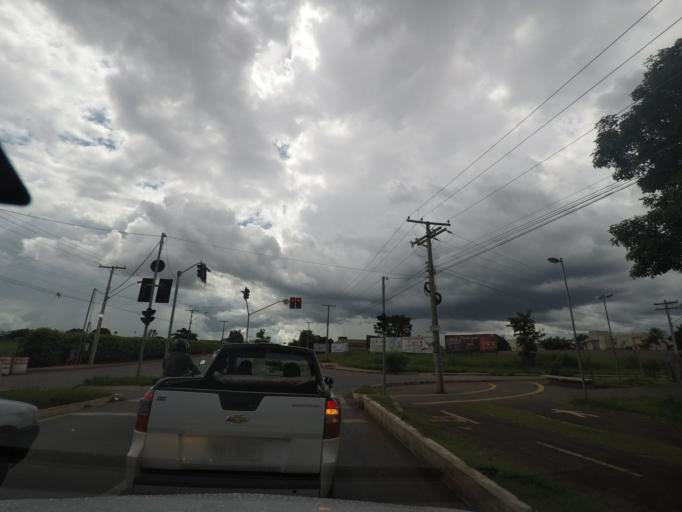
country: BR
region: Goias
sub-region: Goiania
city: Goiania
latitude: -16.7200
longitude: -49.3258
